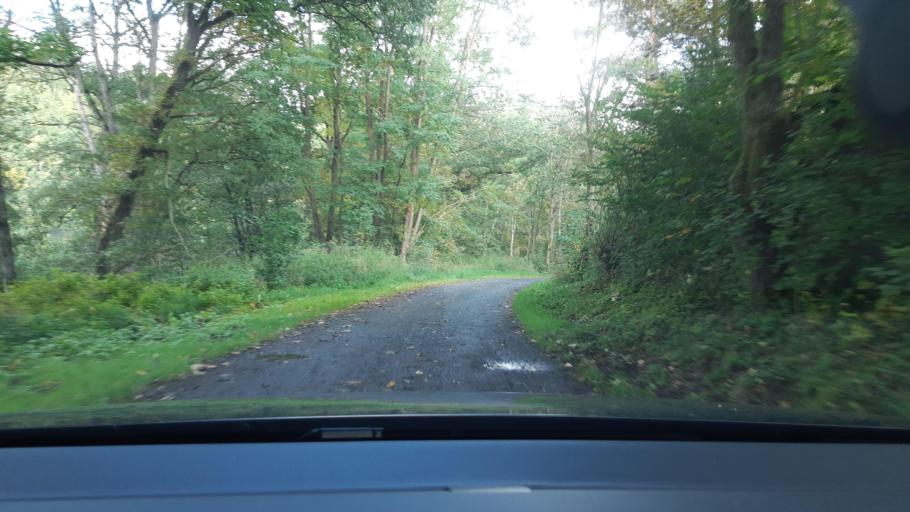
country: DE
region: Hesse
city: Herborn
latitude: 50.6771
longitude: 8.3197
